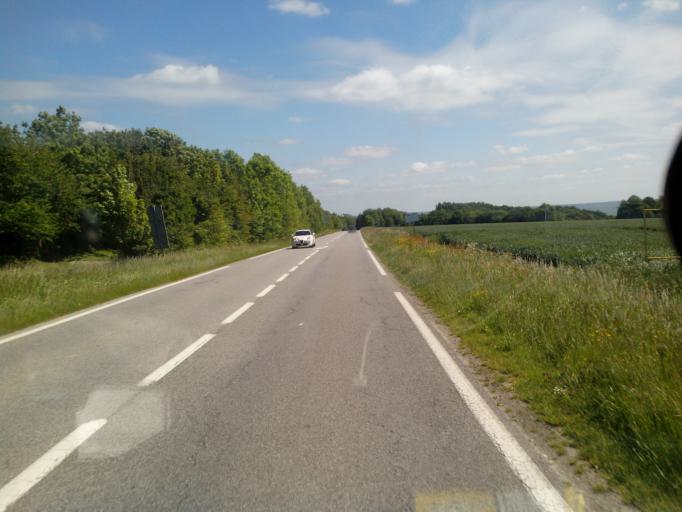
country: FR
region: Haute-Normandie
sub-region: Departement de la Seine-Maritime
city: Tancarville
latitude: 49.4956
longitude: 0.4373
